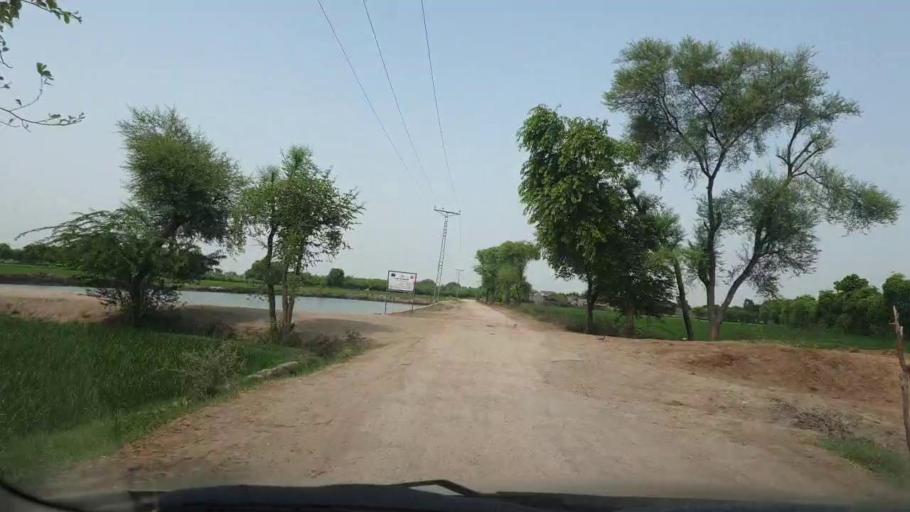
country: PK
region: Sindh
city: Larkana
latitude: 27.5838
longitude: 68.1442
